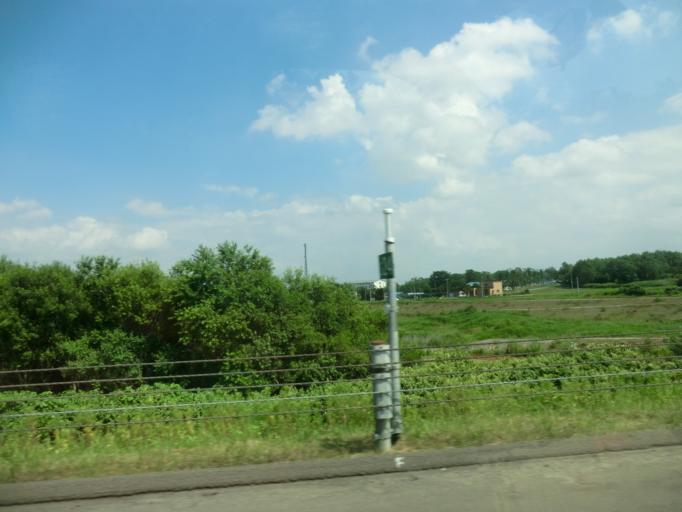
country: JP
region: Hokkaido
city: Kitahiroshima
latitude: 42.8918
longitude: 141.5494
